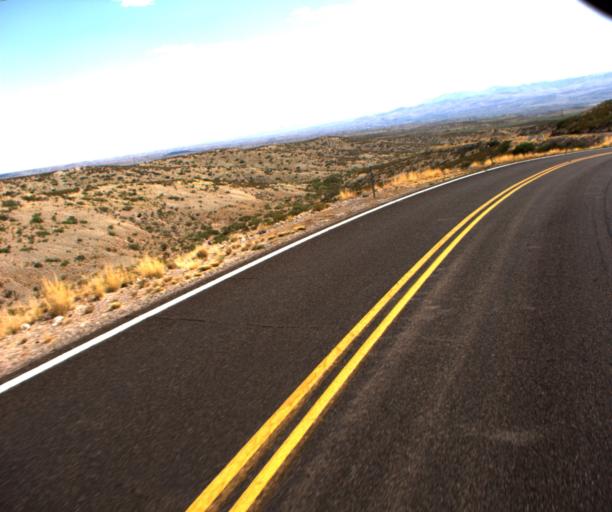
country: US
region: Arizona
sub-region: Greenlee County
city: Clifton
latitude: 32.9969
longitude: -109.1755
